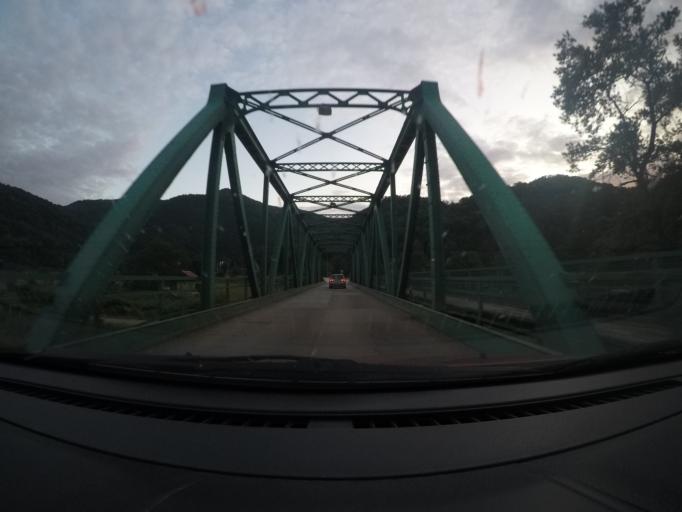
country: RS
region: Central Serbia
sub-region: Moravicki Okrug
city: Lucani
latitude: 43.8999
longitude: 20.1894
